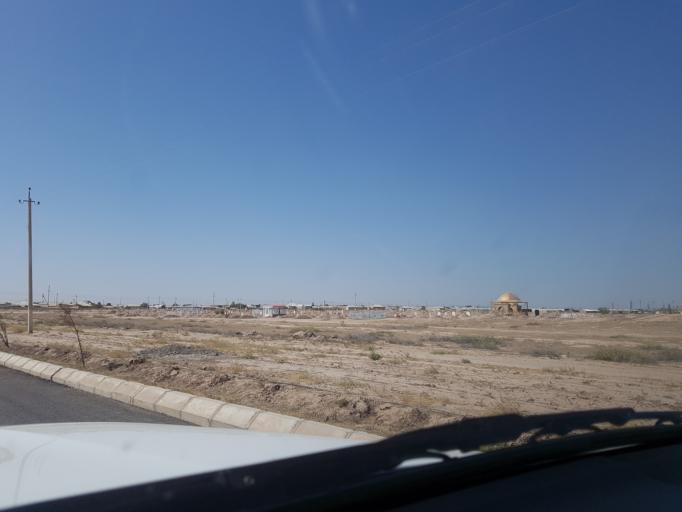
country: IR
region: Razavi Khorasan
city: Sarakhs
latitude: 36.5138
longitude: 61.2287
